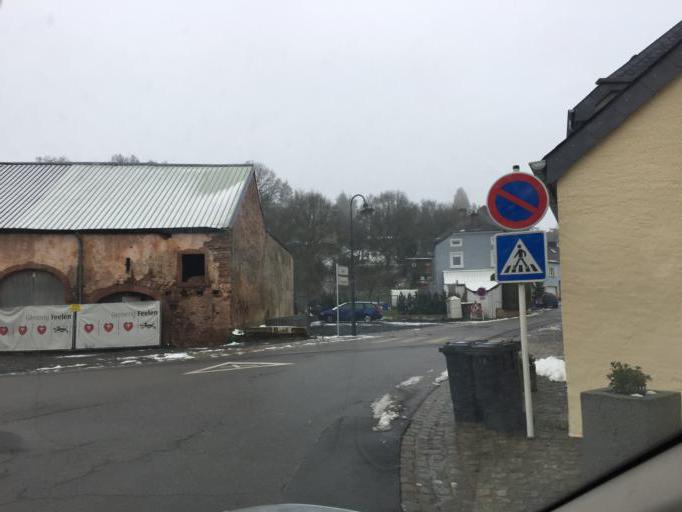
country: LU
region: Diekirch
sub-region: Canton de Diekirch
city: Niederfeulen
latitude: 49.8557
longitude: 6.0463
